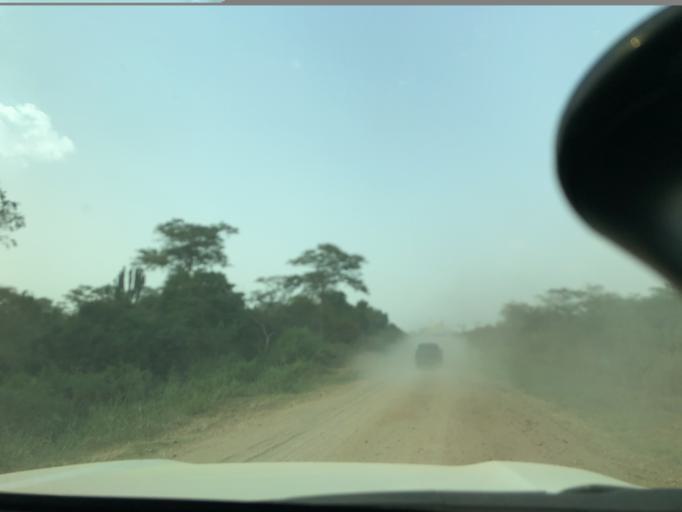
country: CD
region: Nord Kivu
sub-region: North Kivu
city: Butembo
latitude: 0.1409
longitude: 29.6438
